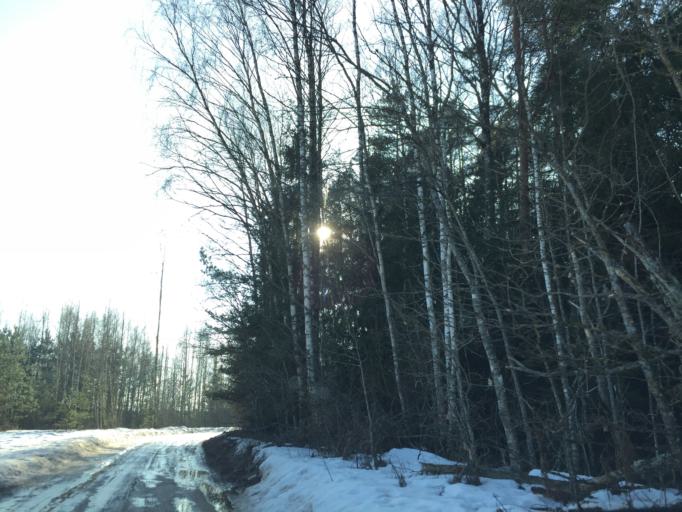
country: LV
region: Lecava
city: Iecava
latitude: 56.6773
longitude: 24.1965
